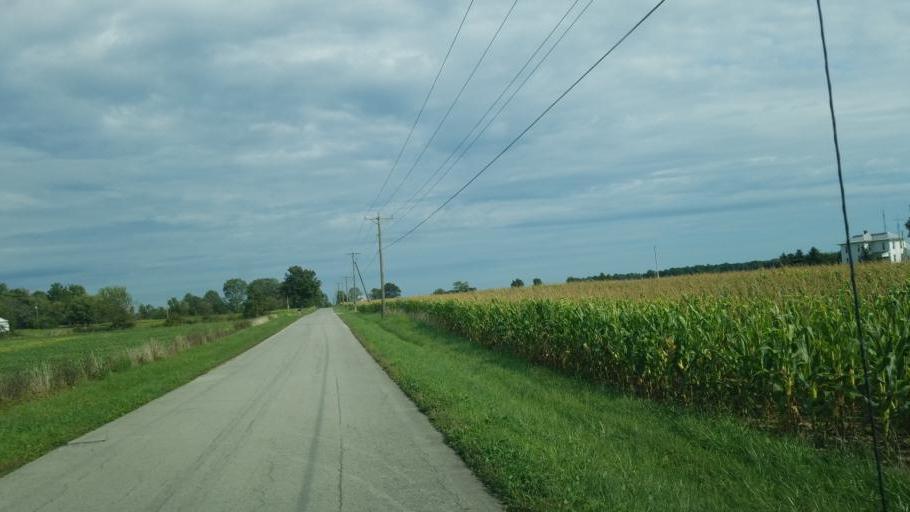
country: US
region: Ohio
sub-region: Hancock County
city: Arlington
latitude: 40.8774
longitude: -83.6305
